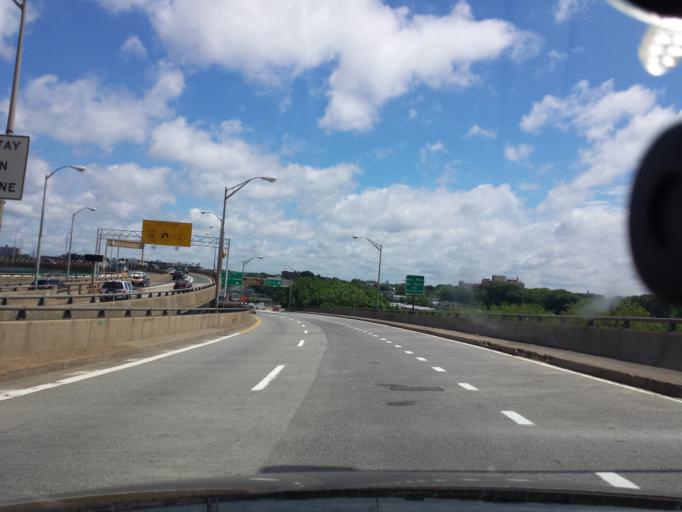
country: US
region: New York
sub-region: Kings County
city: Bensonhurst
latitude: 40.6118
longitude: -74.0295
